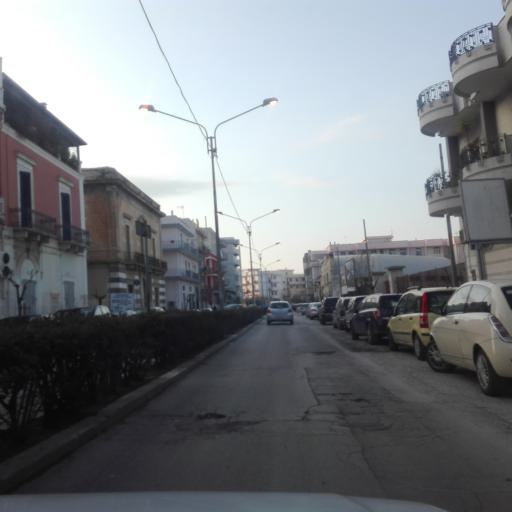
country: IT
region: Apulia
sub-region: Provincia di Bari
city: Corato
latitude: 41.1561
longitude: 16.4162
